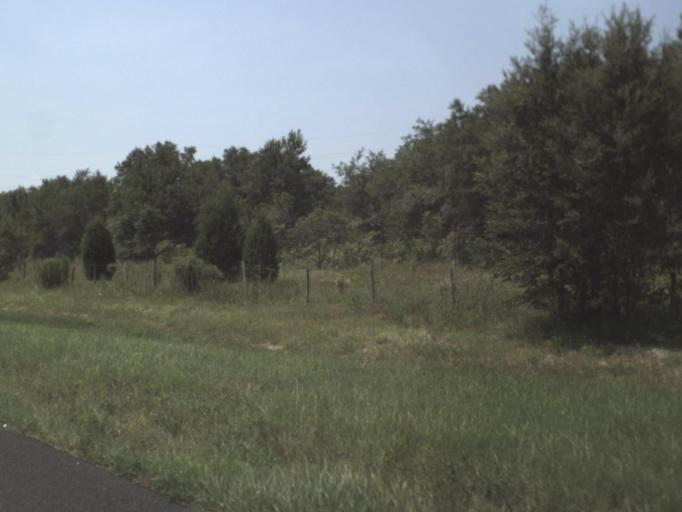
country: US
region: Florida
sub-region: Levy County
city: Inglis
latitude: 28.9986
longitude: -82.6541
